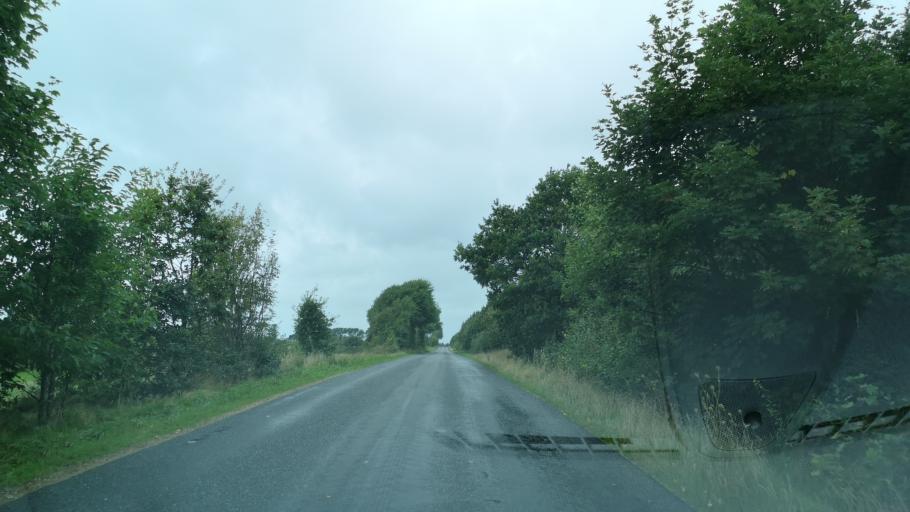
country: DK
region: Central Jutland
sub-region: Ringkobing-Skjern Kommune
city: Videbaek
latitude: 56.0595
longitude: 8.6758
